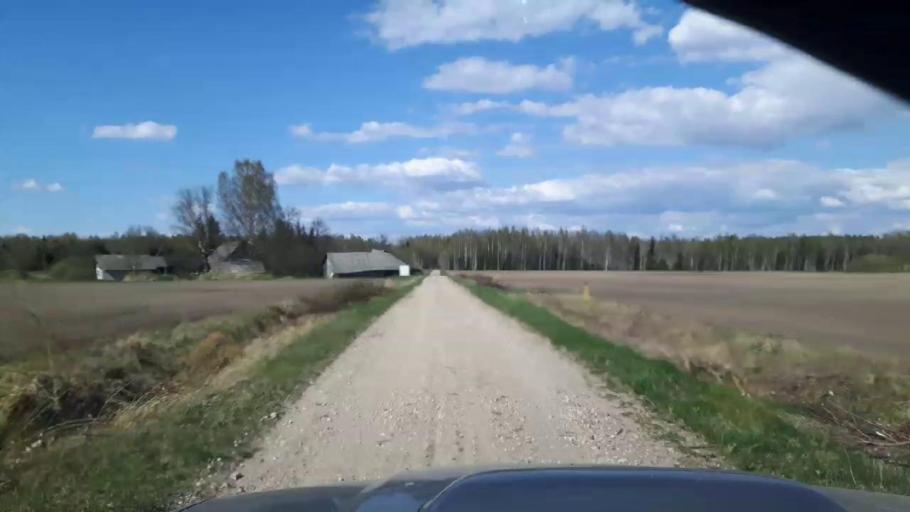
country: EE
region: Paernumaa
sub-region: Tootsi vald
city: Tootsi
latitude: 58.4532
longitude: 24.8453
